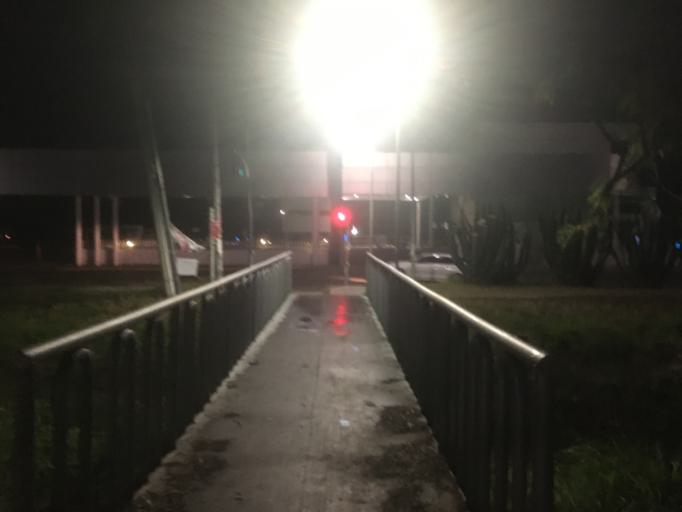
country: MX
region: Queretaro
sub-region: Queretaro
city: Santiago de Queretaro
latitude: 20.6119
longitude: -100.4035
